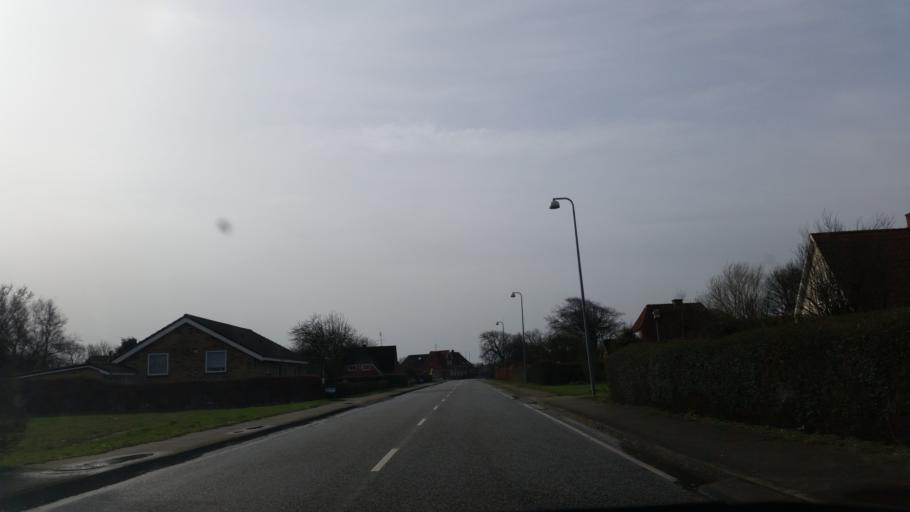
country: DK
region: South Denmark
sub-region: Tonder Kommune
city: Sherrebek
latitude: 55.0770
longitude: 8.6763
